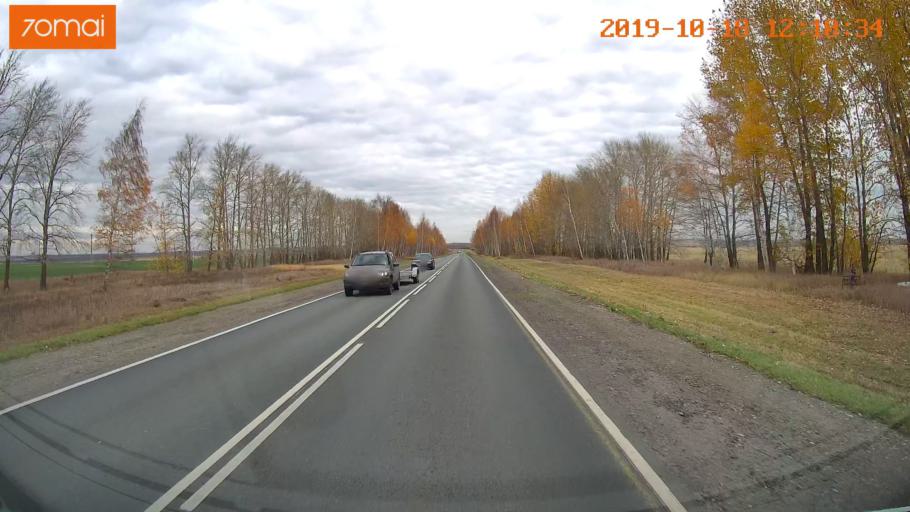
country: RU
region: Rjazan
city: Zakharovo
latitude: 54.3935
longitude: 39.3339
